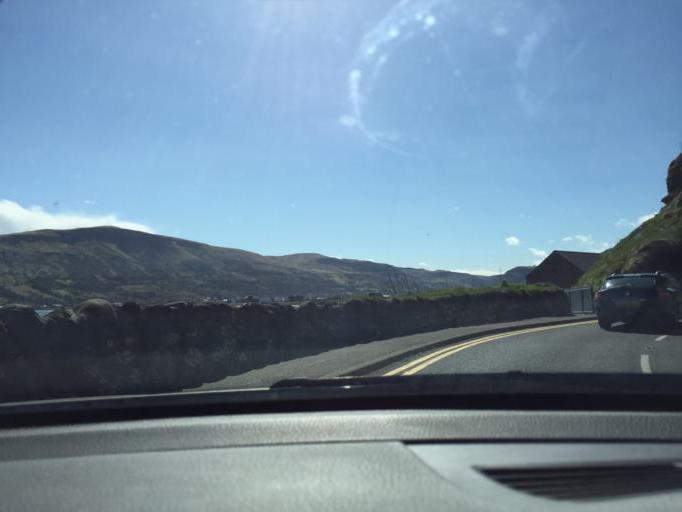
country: GB
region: Northern Ireland
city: Cushendall
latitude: 55.0671
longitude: -6.0543
